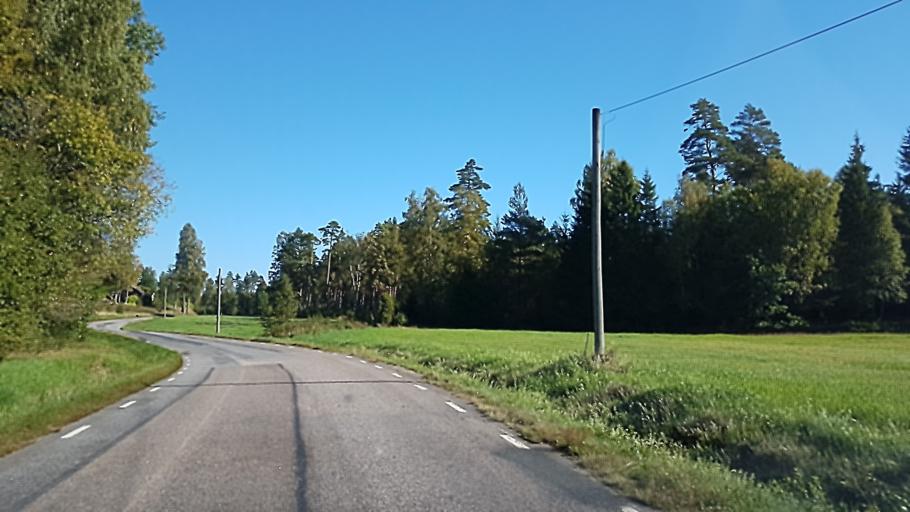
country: SE
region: Kronoberg
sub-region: Ljungby Kommun
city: Ljungby
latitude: 56.8124
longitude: 14.0352
